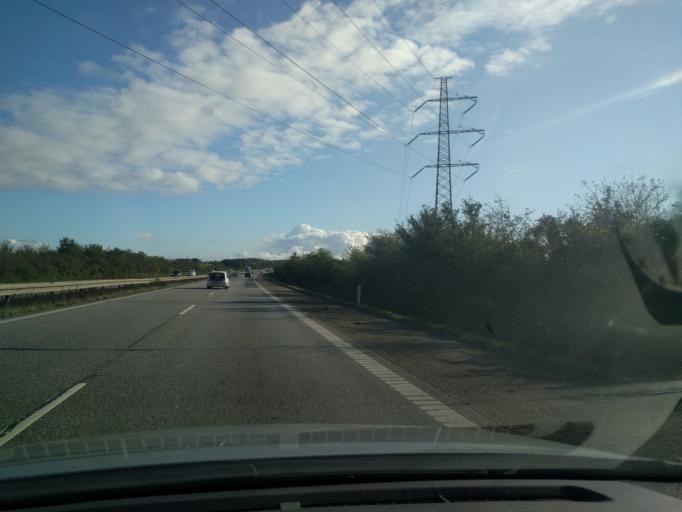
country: DK
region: Zealand
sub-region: Ringsted Kommune
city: Ringsted
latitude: 55.4550
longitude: 11.7494
